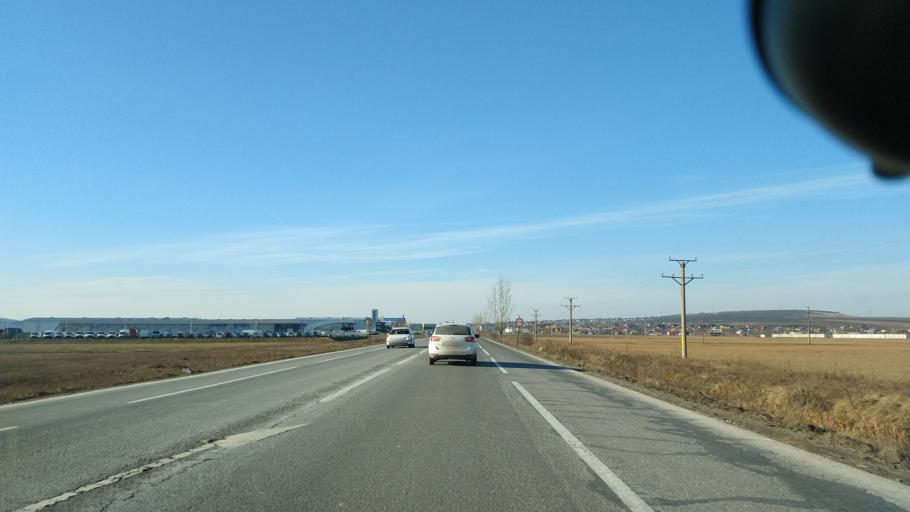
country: RO
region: Iasi
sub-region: Comuna Letcani
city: Letcani
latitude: 47.1878
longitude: 27.4405
